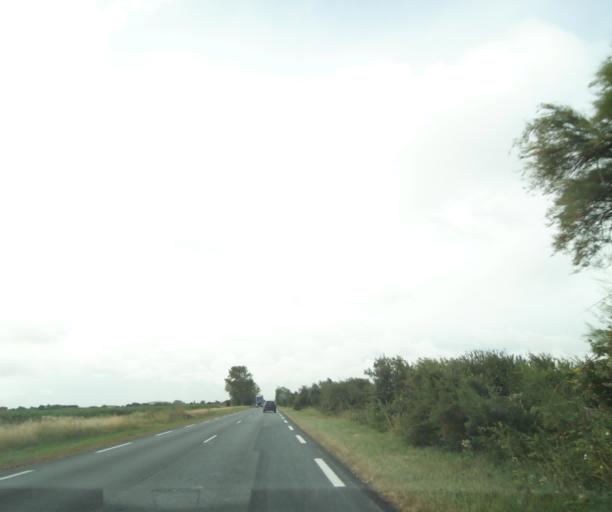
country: FR
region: Poitou-Charentes
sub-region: Departement de la Charente-Maritime
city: Andilly
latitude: 46.2582
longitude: -1.0667
